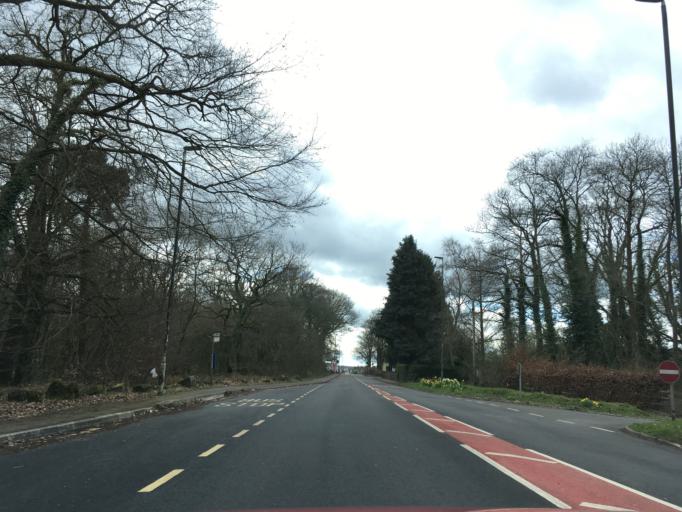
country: GB
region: England
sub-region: Gloucestershire
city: Coleford
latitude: 51.8092
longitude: -2.6068
